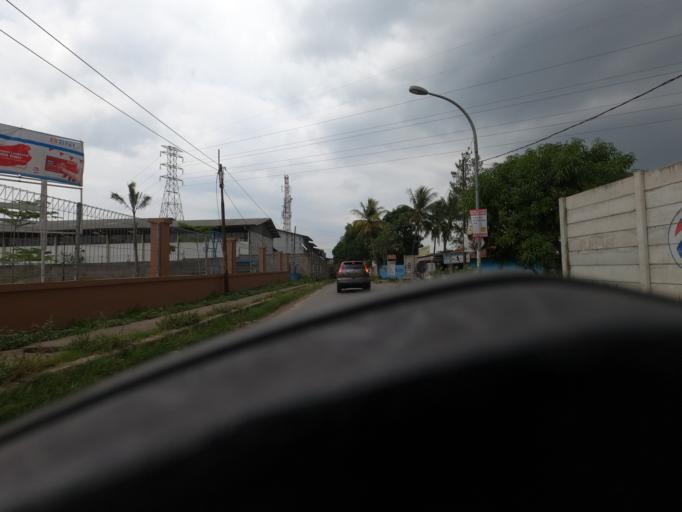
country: ID
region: West Java
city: Padalarang
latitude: -6.8466
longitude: 107.4926
